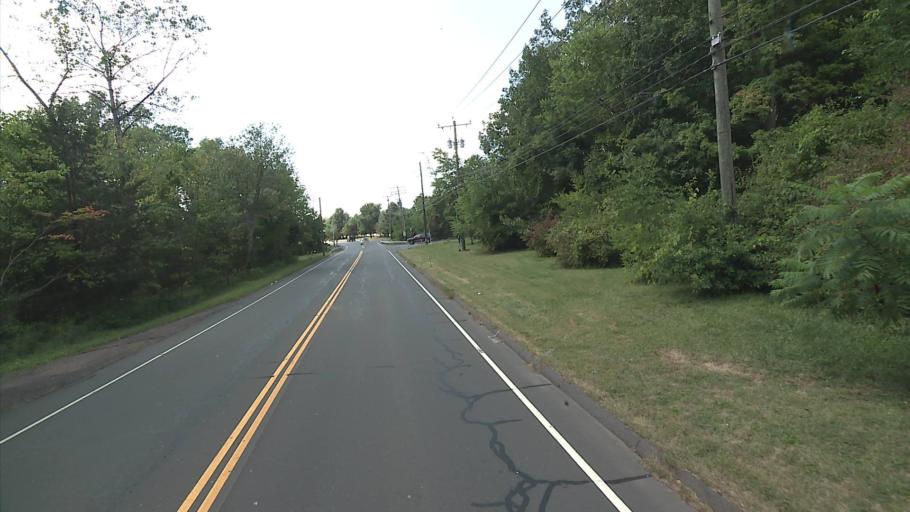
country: US
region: Connecticut
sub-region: Hartford County
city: Kensington
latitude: 41.6426
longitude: -72.7259
